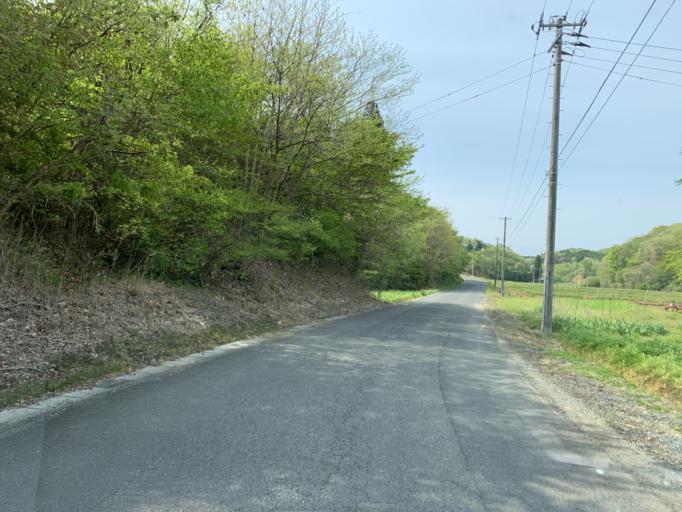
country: JP
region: Iwate
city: Ichinoseki
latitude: 38.8949
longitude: 141.0618
